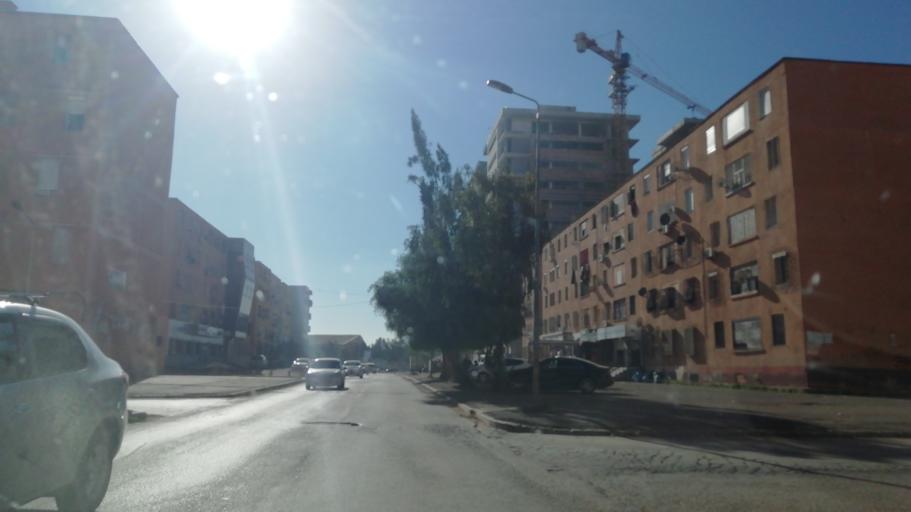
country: DZ
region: Oran
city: Oran
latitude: 35.6676
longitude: -0.6473
